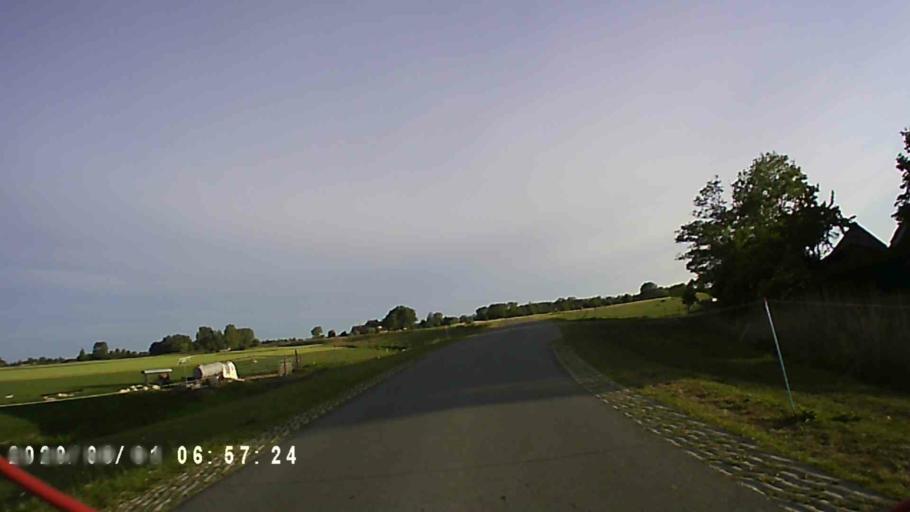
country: NL
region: Friesland
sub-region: Gemeente Dongeradeel
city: Anjum
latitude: 53.3180
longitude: 6.1074
